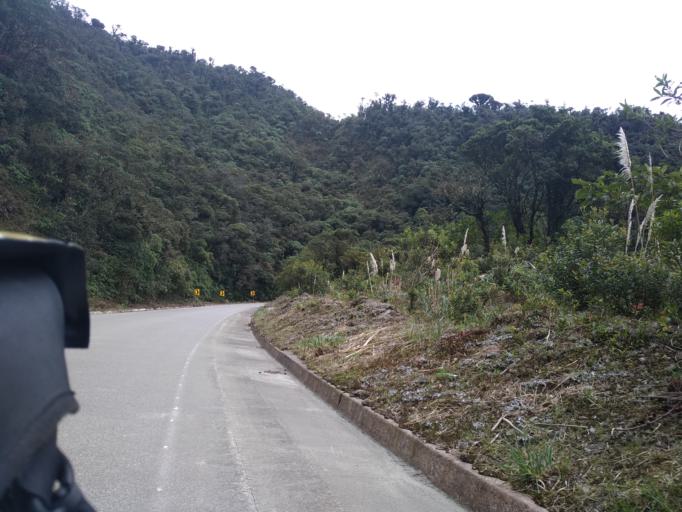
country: EC
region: Zamora-Chinchipe
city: Zamora
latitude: -4.4335
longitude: -79.1490
